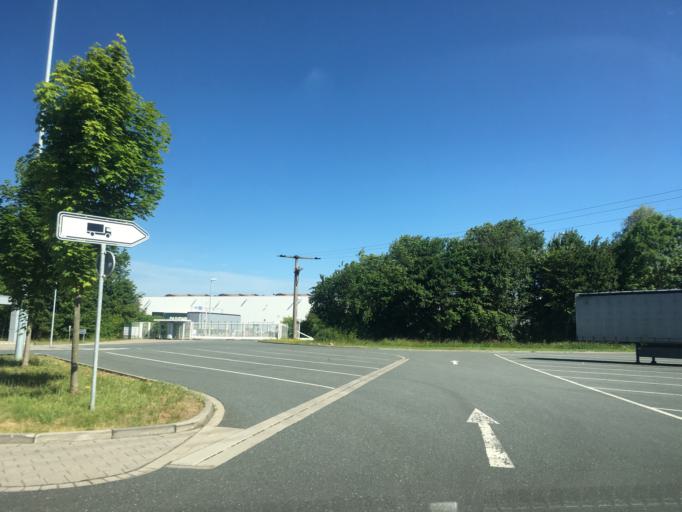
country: DE
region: North Rhine-Westphalia
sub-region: Regierungsbezirk Munster
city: Altenberge
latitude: 52.0310
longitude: 7.4514
